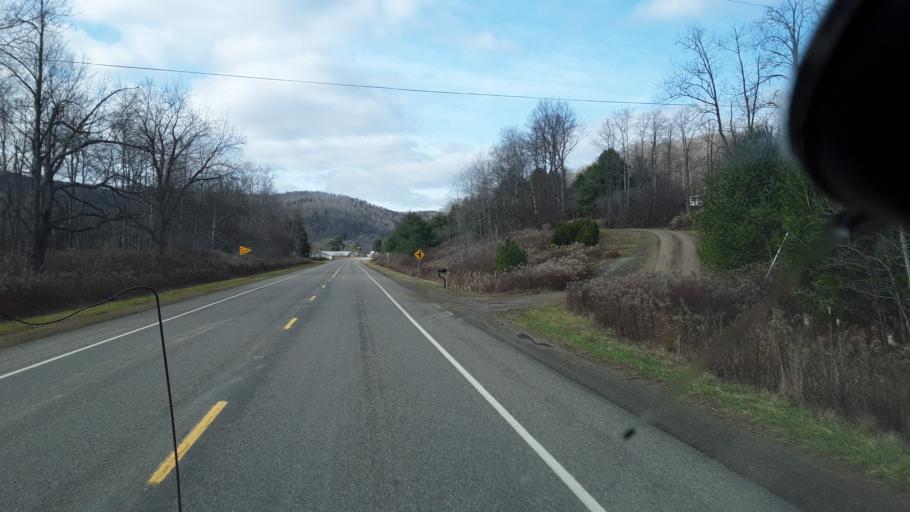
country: US
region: Pennsylvania
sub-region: Potter County
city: Galeton
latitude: 41.7772
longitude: -77.7181
